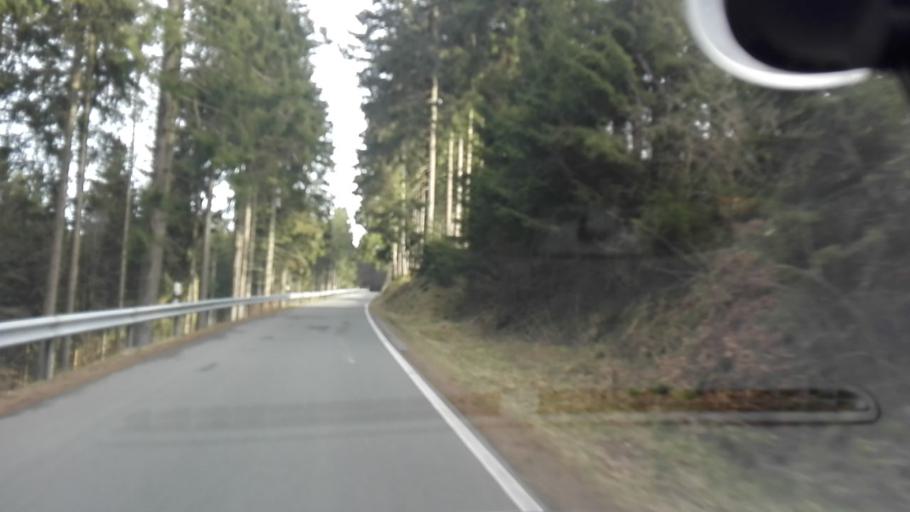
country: DE
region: North Rhine-Westphalia
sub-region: Regierungsbezirk Arnsberg
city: Schmallenberg
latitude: 51.1365
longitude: 8.3463
